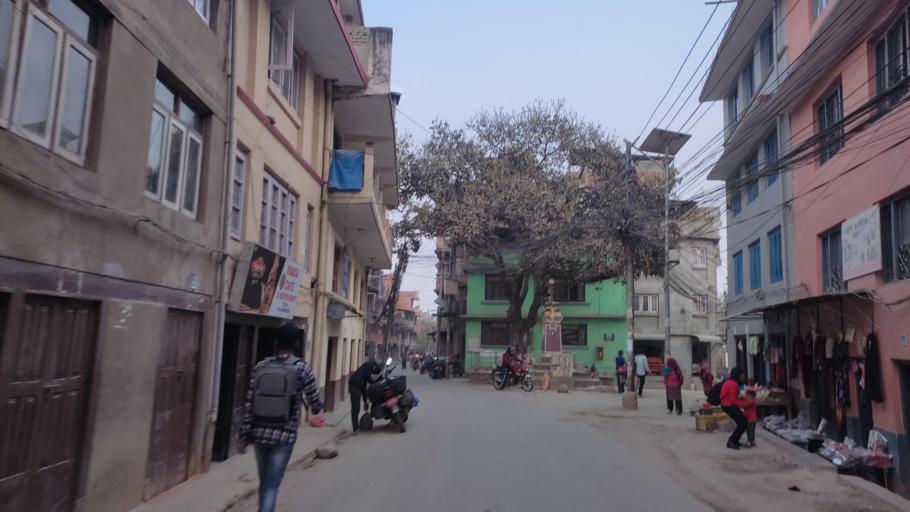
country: NP
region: Central Region
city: Kirtipur
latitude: 27.6701
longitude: 85.2810
